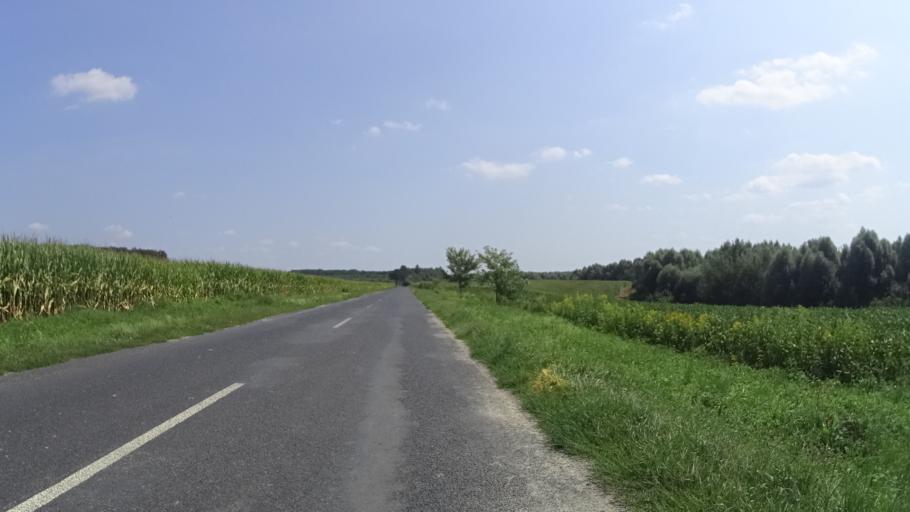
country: HU
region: Zala
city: Murakeresztur
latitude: 46.3735
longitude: 16.8539
